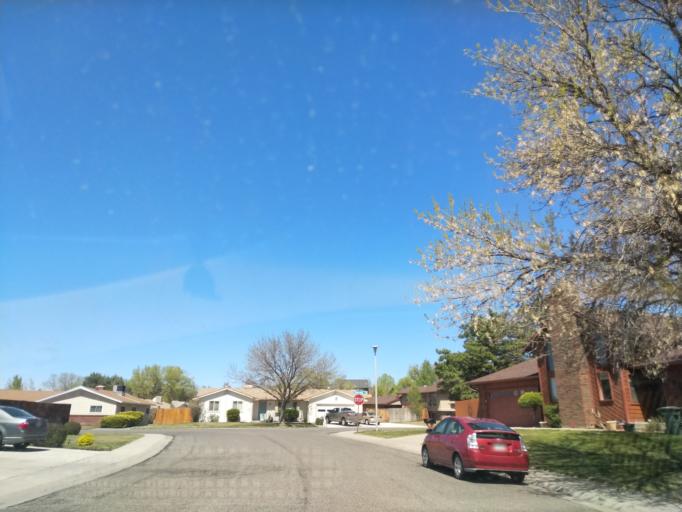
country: US
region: Colorado
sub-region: Mesa County
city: Grand Junction
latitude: 39.0952
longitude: -108.5412
